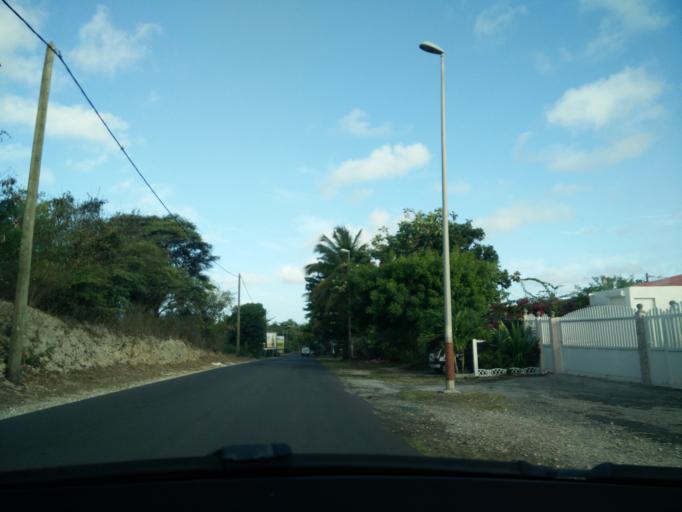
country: GP
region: Guadeloupe
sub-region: Guadeloupe
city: Le Moule
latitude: 16.3249
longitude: -61.3494
